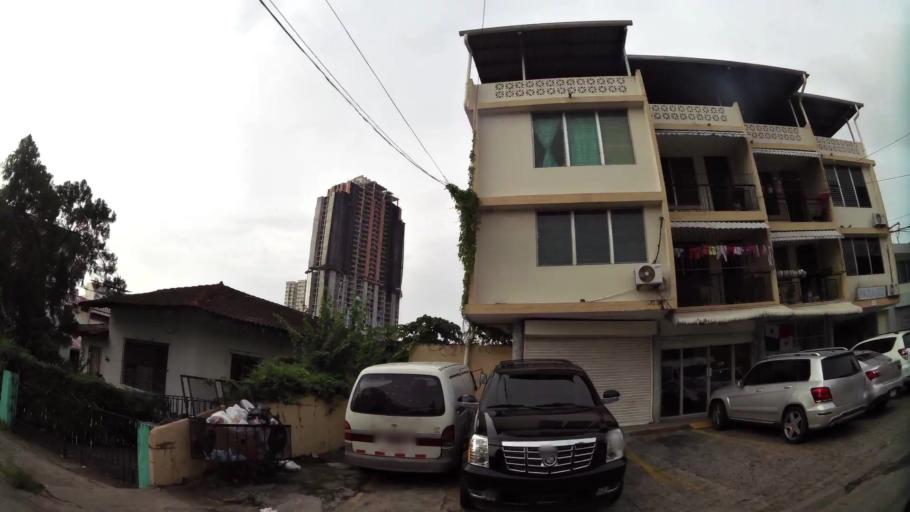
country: PA
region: Panama
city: Panama
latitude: 8.9948
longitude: -79.5175
